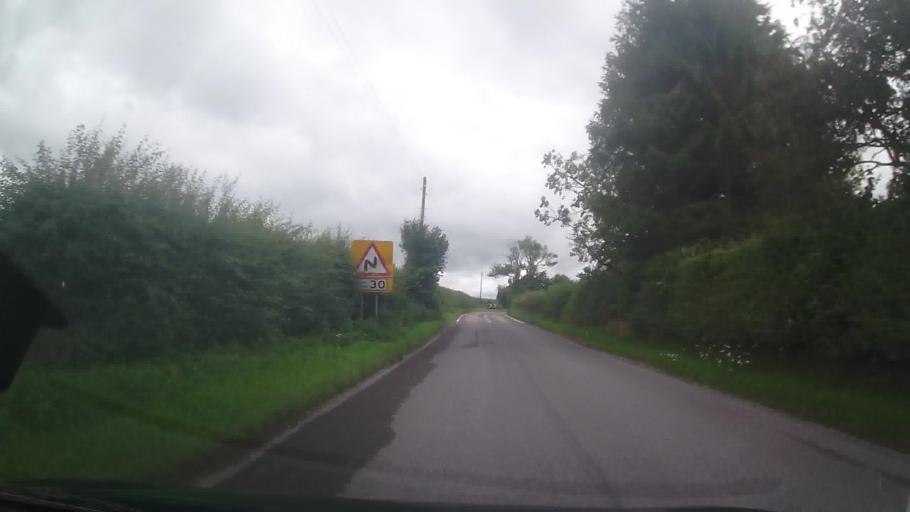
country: GB
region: England
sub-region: Shropshire
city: Petton
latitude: 52.8395
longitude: -2.8204
